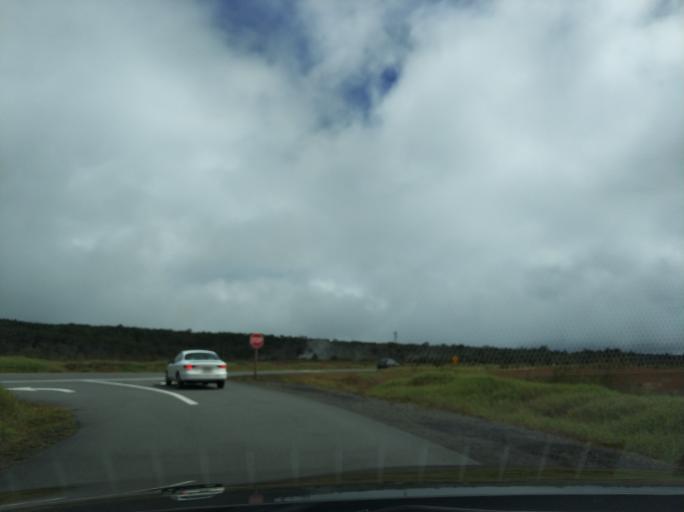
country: US
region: Hawaii
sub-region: Hawaii County
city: Volcano
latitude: 19.4315
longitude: -155.2671
